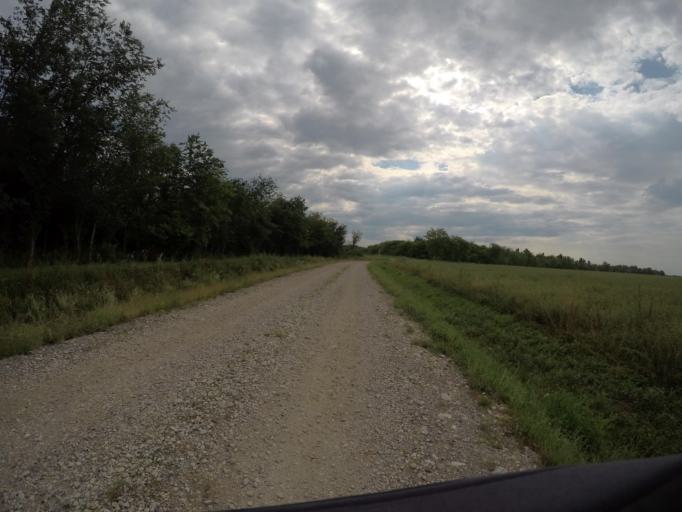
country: IT
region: Friuli Venezia Giulia
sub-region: Provincia di Udine
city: Trivignano Udinese
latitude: 45.9428
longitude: 13.3153
